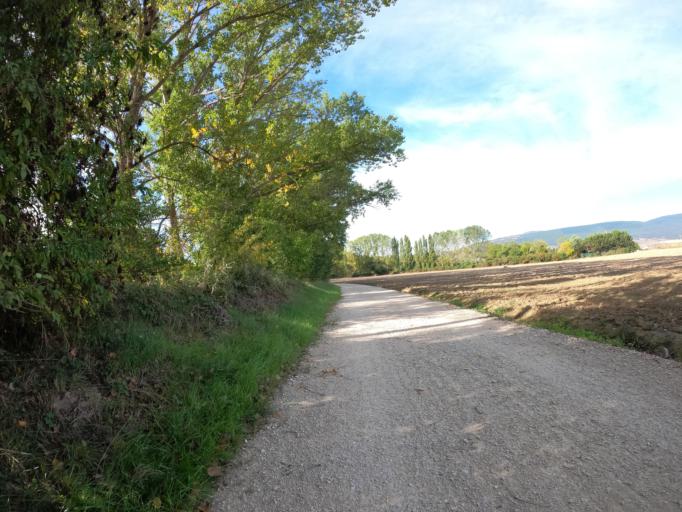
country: ES
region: Navarre
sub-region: Provincia de Navarra
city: Oltza
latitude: 42.8138
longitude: -1.7501
